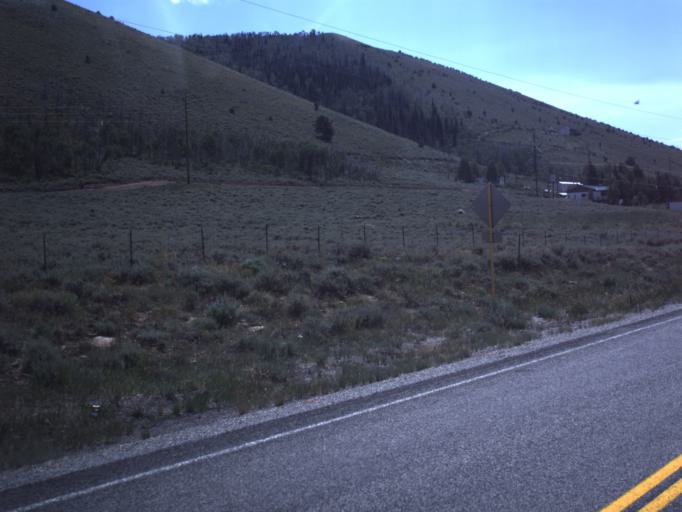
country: US
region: Utah
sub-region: Carbon County
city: Helper
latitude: 39.8152
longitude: -111.1354
